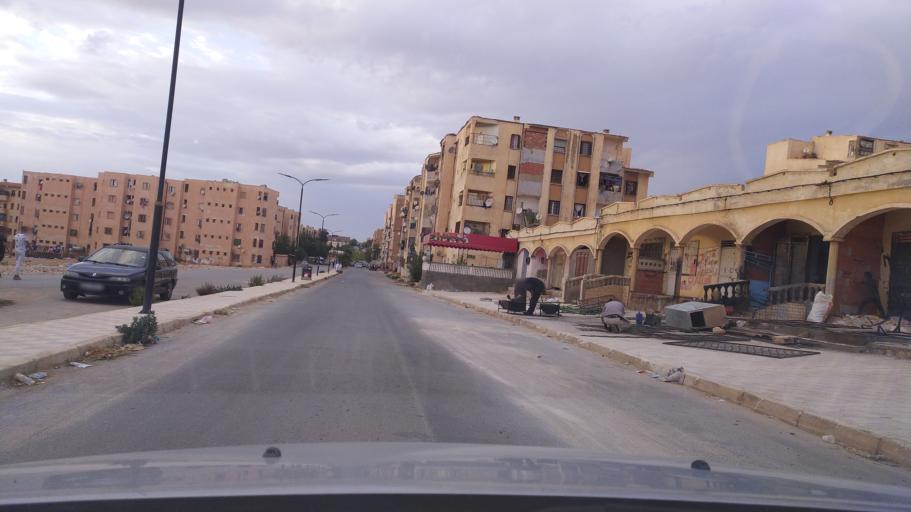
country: DZ
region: Tiaret
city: Frenda
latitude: 35.0547
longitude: 1.0625
